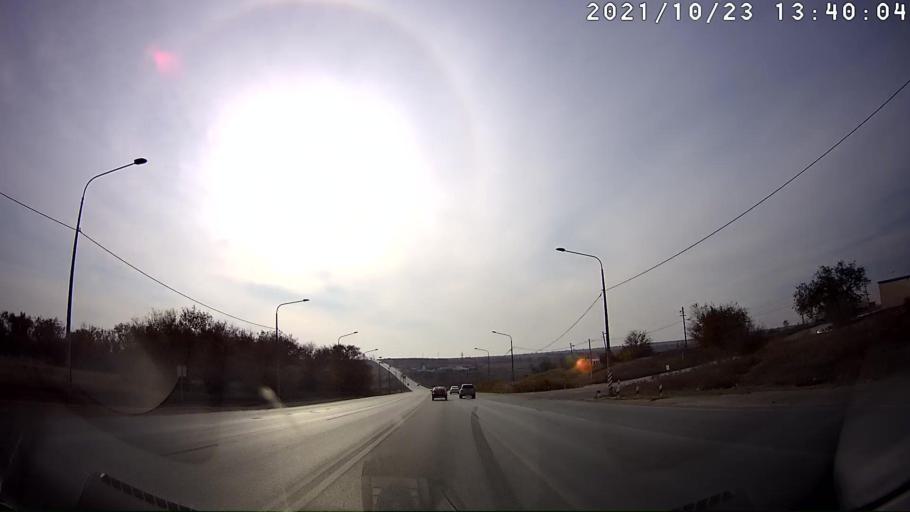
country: RU
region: Volgograd
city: Vodstroy
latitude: 48.8373
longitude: 44.5420
